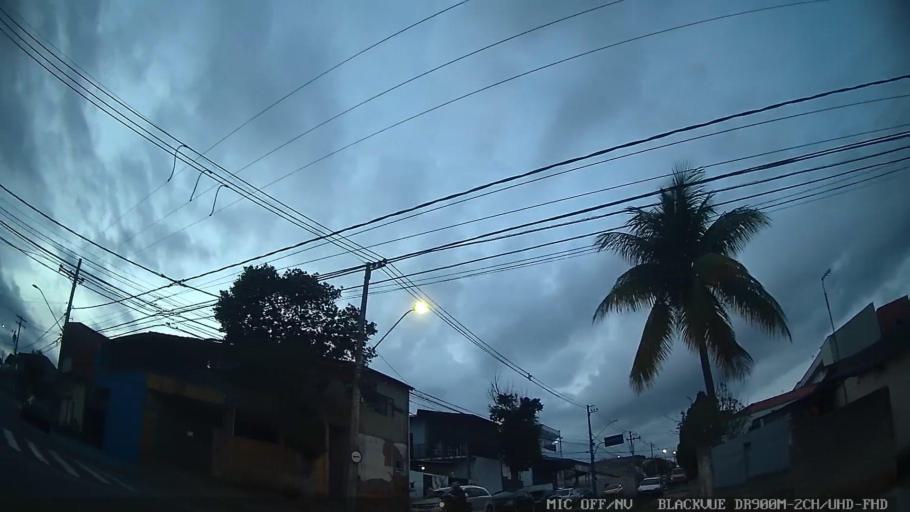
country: BR
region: Sao Paulo
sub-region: Indaiatuba
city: Indaiatuba
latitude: -23.1302
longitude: -47.2395
